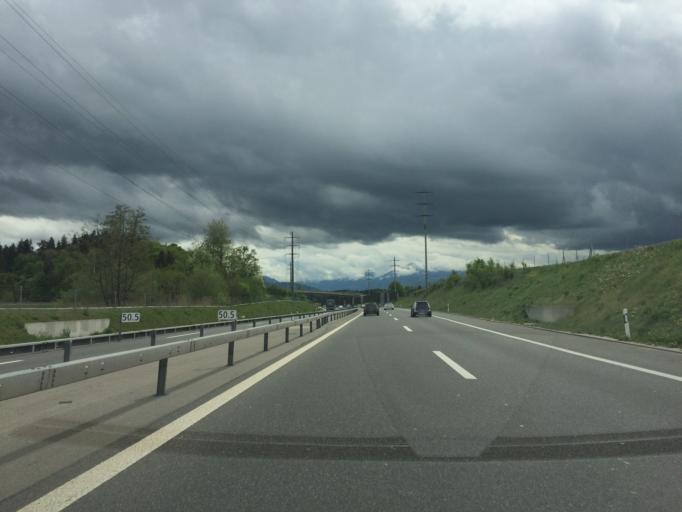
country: CH
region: Zurich
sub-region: Bezirk Affoltern
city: Obfelden / Toussen
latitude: 47.2626
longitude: 8.4412
